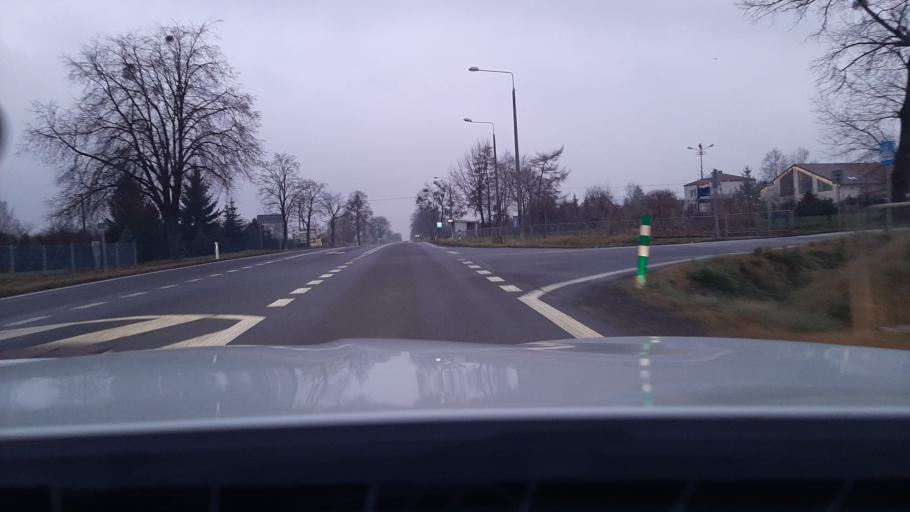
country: PL
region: Lublin Voivodeship
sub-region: Powiat lubelski
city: Garbow
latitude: 51.3439
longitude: 22.3634
